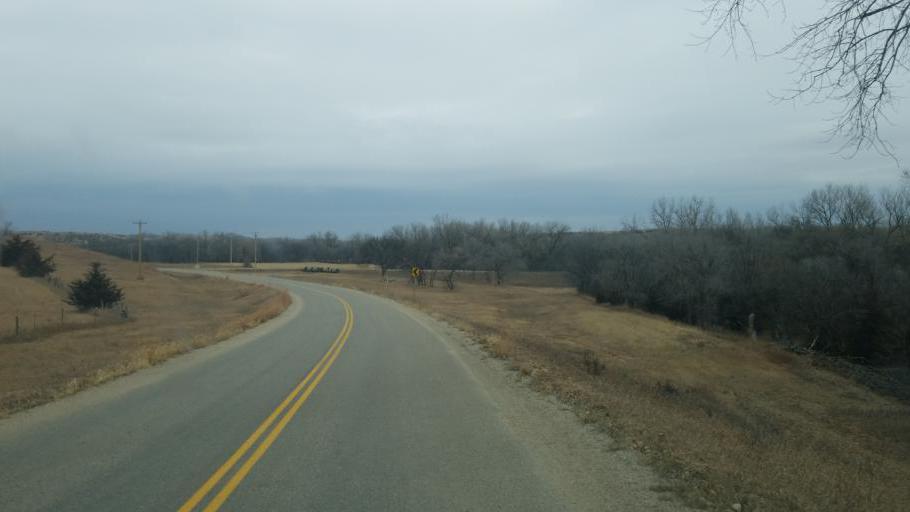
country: US
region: Nebraska
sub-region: Knox County
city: Center
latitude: 42.6668
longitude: -97.8872
